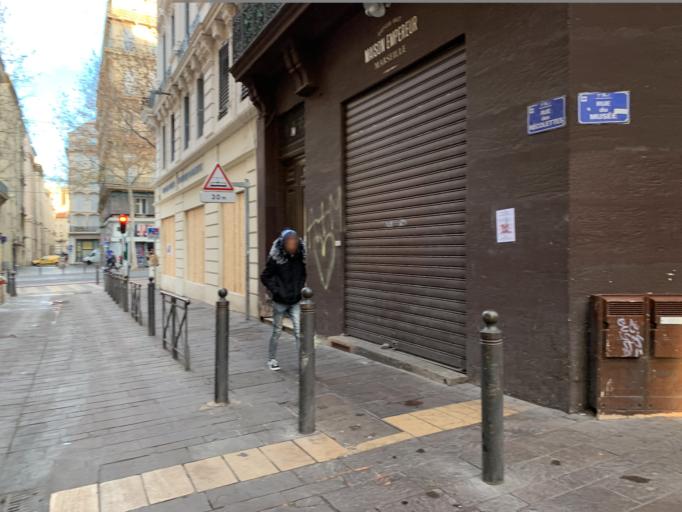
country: FR
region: Provence-Alpes-Cote d'Azur
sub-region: Departement des Bouches-du-Rhone
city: Marseille
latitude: 43.2962
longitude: 5.3784
